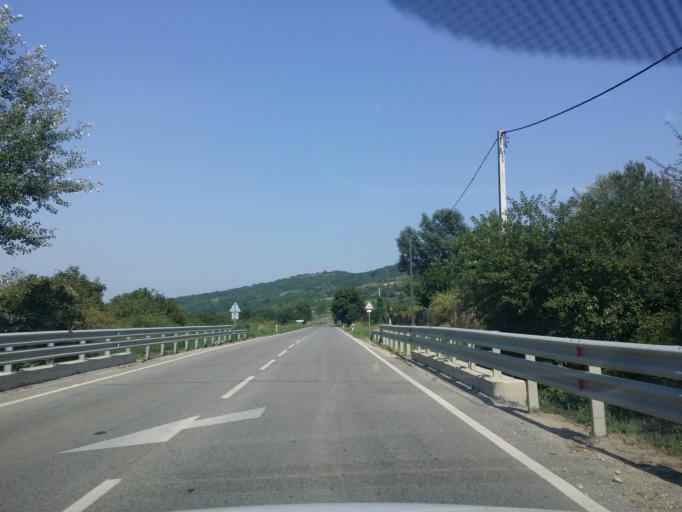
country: HU
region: Tolna
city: Pincehely
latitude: 46.6942
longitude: 18.4589
